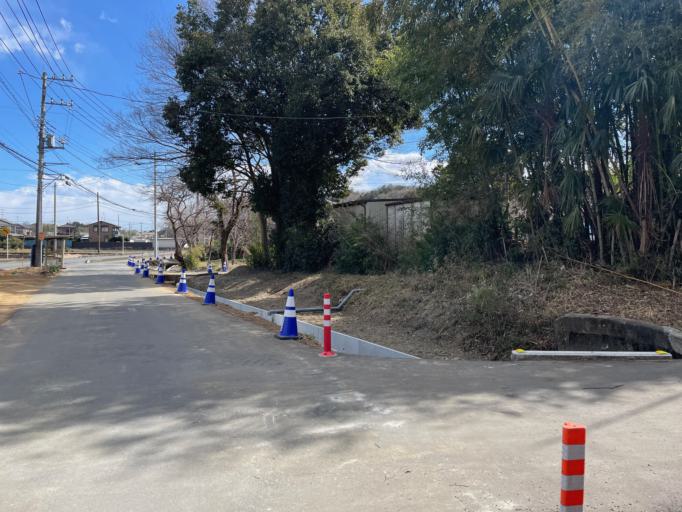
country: JP
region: Saitama
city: Sakado
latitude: 36.0185
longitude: 139.3783
